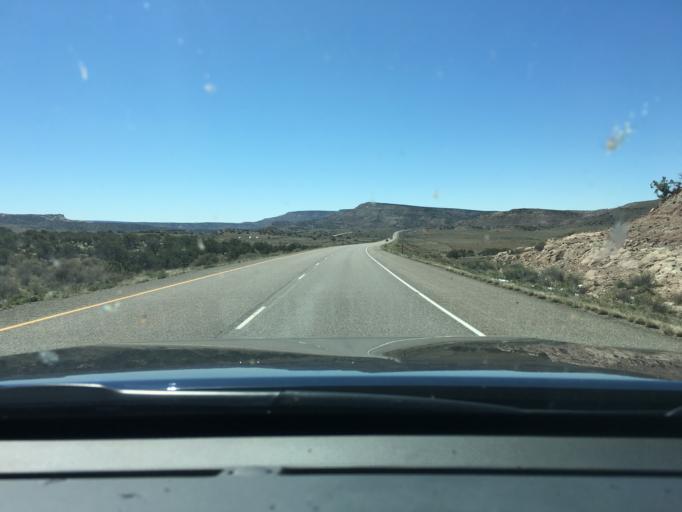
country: US
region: Colorado
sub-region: Mesa County
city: Loma
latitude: 39.2032
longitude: -108.9870
